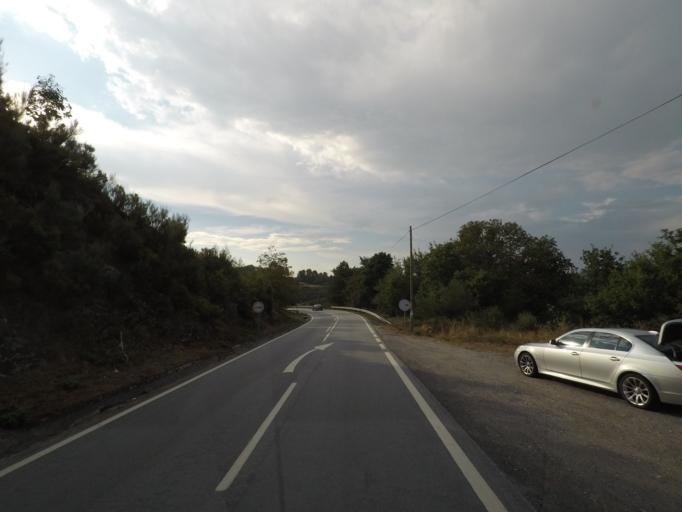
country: PT
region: Porto
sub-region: Baiao
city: Valadares
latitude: 41.2086
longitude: -7.9755
